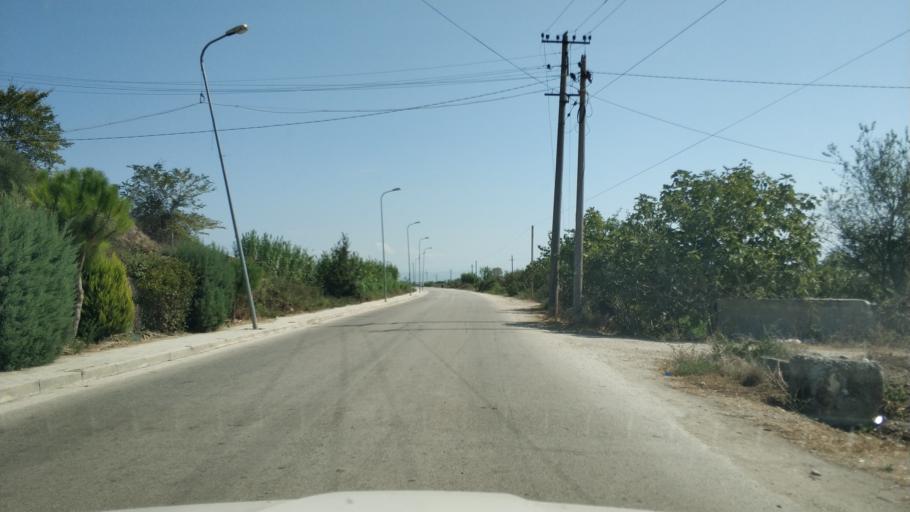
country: AL
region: Fier
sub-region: Rrethi i Lushnjes
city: Gradishte
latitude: 40.8839
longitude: 19.5811
